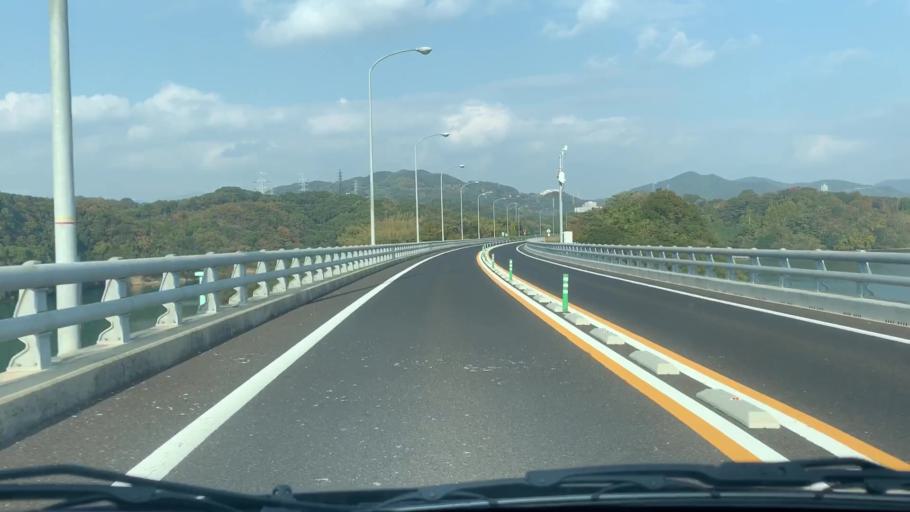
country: JP
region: Nagasaki
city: Sasebo
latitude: 33.0749
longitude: 129.7678
